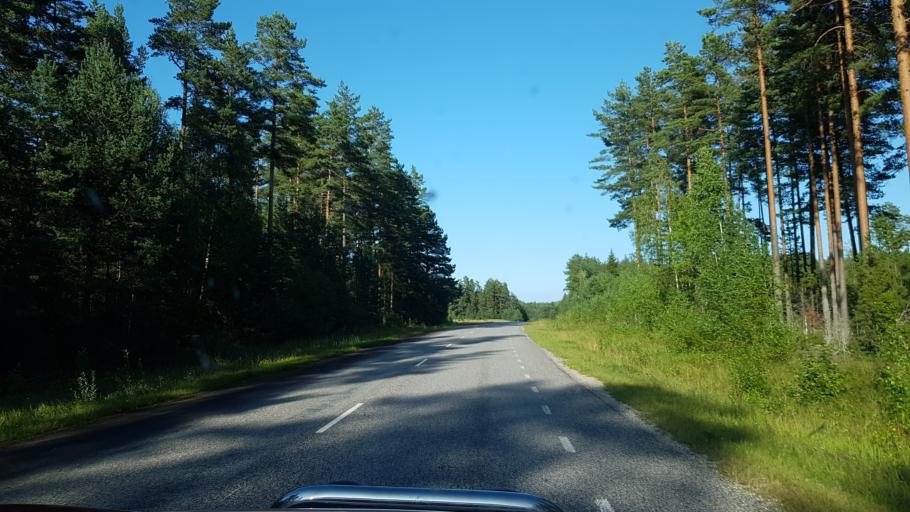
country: RU
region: Pskov
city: Pechory
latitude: 57.8205
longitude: 27.3475
